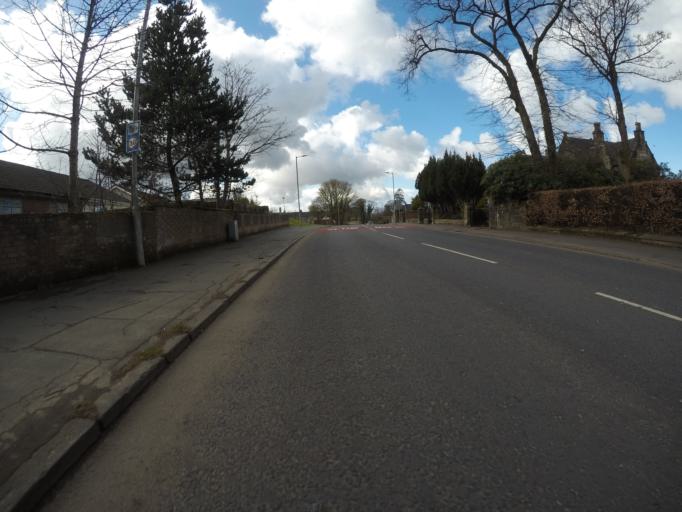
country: GB
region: Scotland
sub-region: North Ayrshire
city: Beith
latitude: 55.7477
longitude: -4.6382
